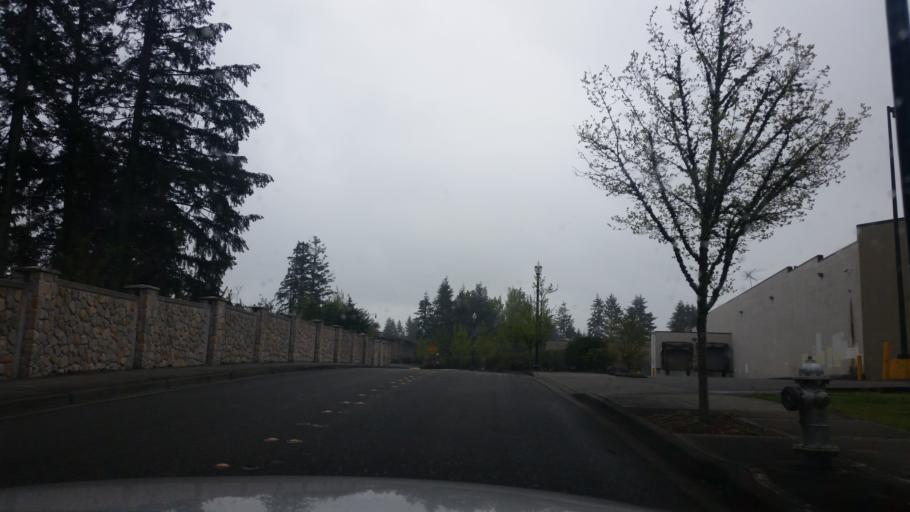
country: US
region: Washington
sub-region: Pierce County
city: University Place
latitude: 47.2225
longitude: -122.5349
